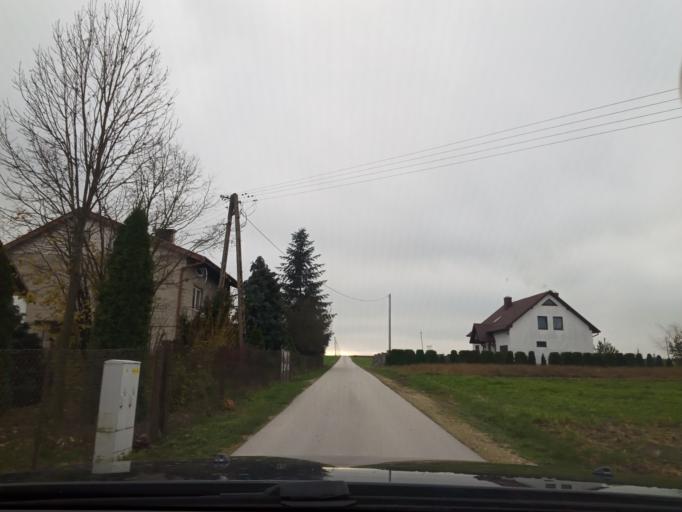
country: PL
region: Swietokrzyskie
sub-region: Powiat jedrzejowski
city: Imielno
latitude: 50.6208
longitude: 20.3964
